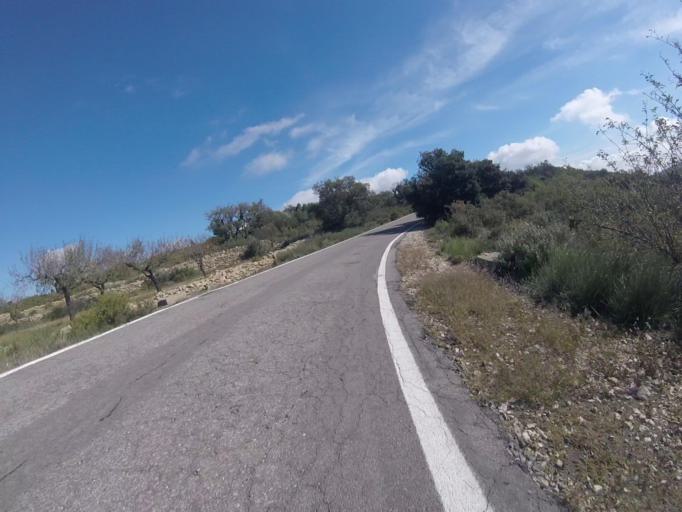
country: ES
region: Valencia
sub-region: Provincia de Castello
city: Albocasser
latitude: 40.3340
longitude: 0.0377
